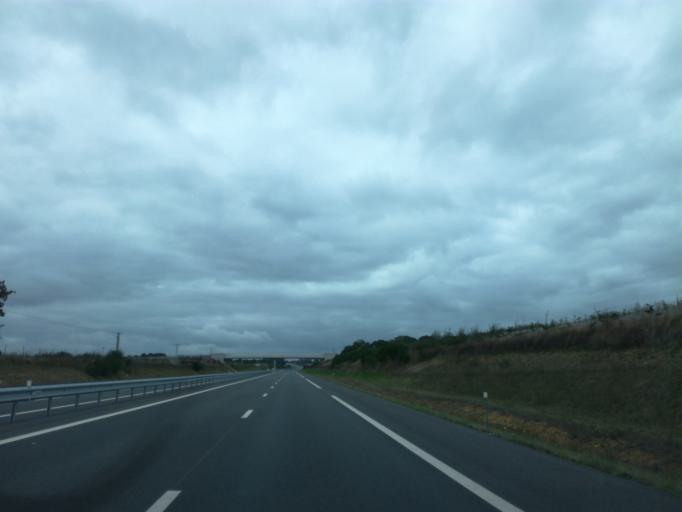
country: FR
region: Brittany
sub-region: Departement d'Ille-et-Vilaine
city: Boisgervilly
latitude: 48.1908
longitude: -2.1161
